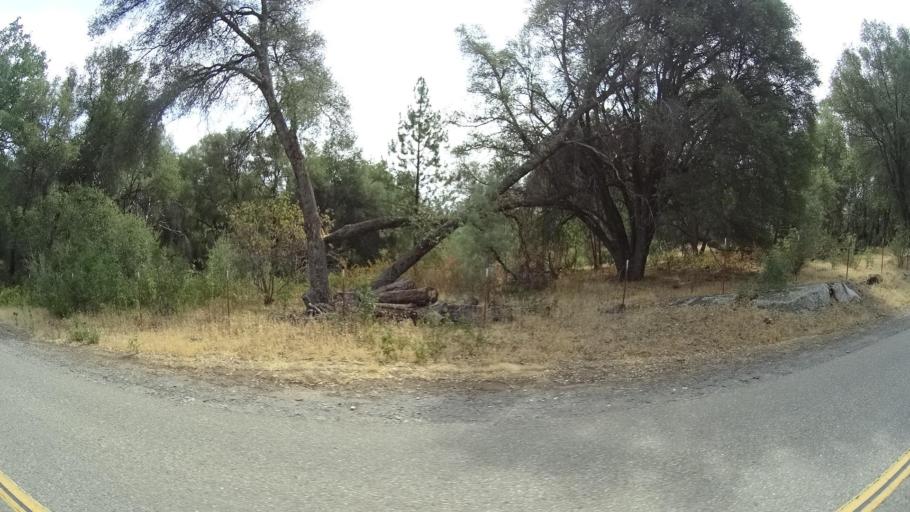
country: US
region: California
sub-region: Mariposa County
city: Mariposa
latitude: 37.4798
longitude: -119.8999
